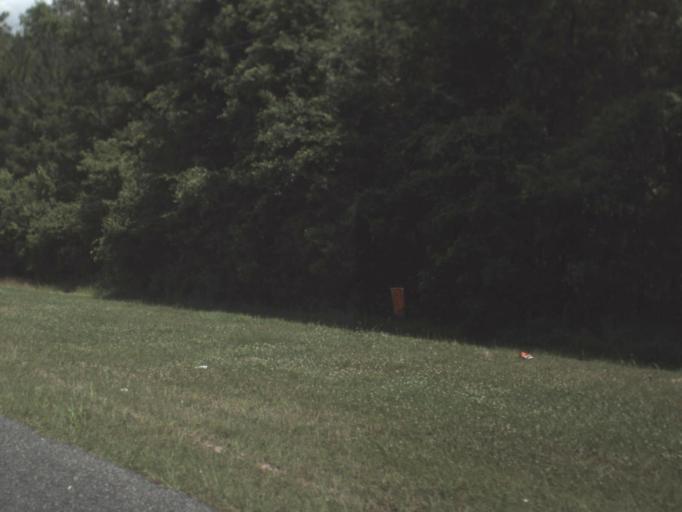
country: US
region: Florida
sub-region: Alachua County
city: Hawthorne
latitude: 29.5986
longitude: -82.1229
